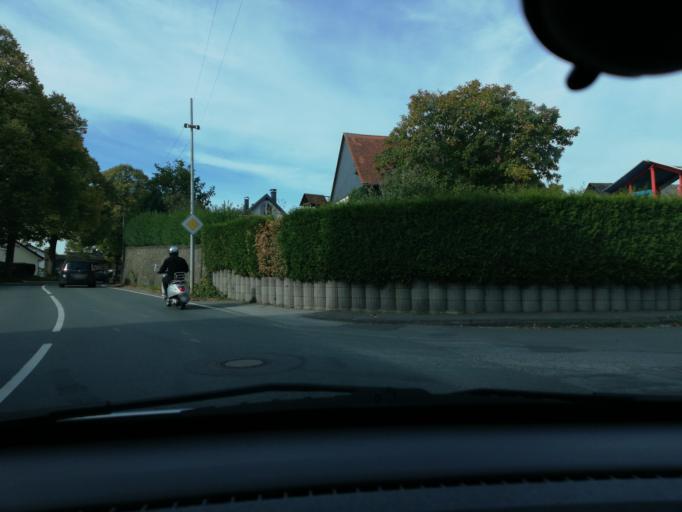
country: DE
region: North Rhine-Westphalia
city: Sprockhovel
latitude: 51.3433
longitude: 7.2591
